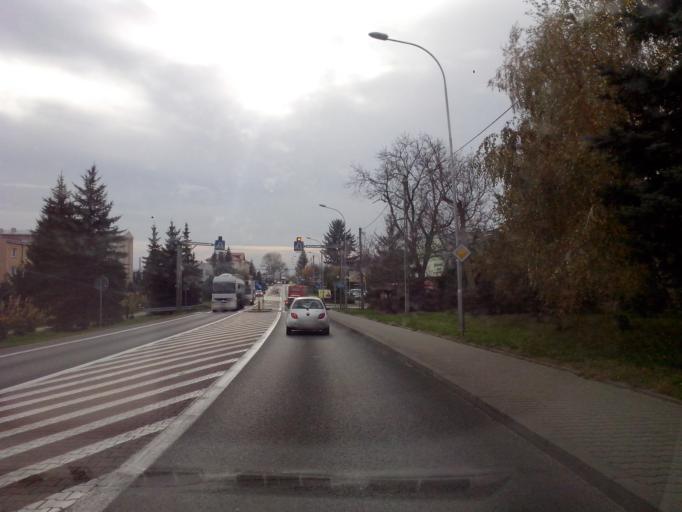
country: PL
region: Subcarpathian Voivodeship
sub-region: Powiat rzeszowski
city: Boguchwala
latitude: 49.9830
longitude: 21.9402
